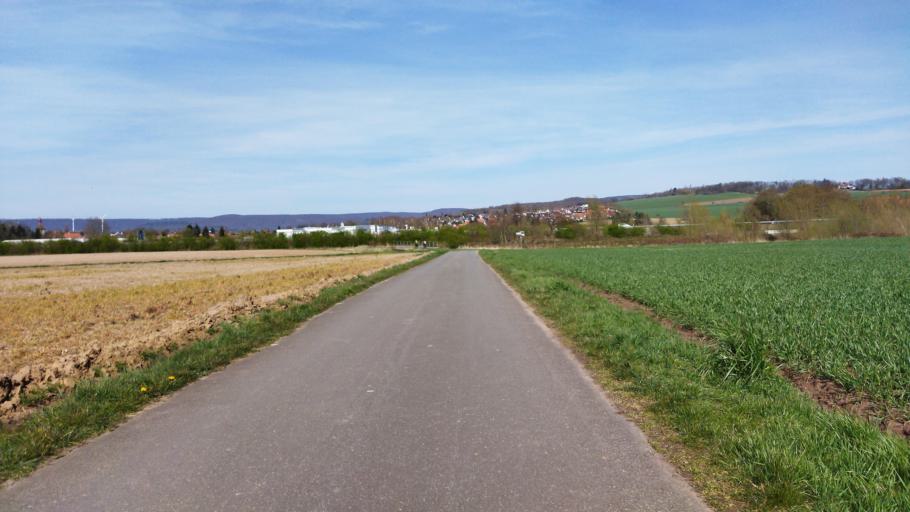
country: DE
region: Lower Saxony
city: Hessisch Oldendorf
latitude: 52.1338
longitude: 9.2948
